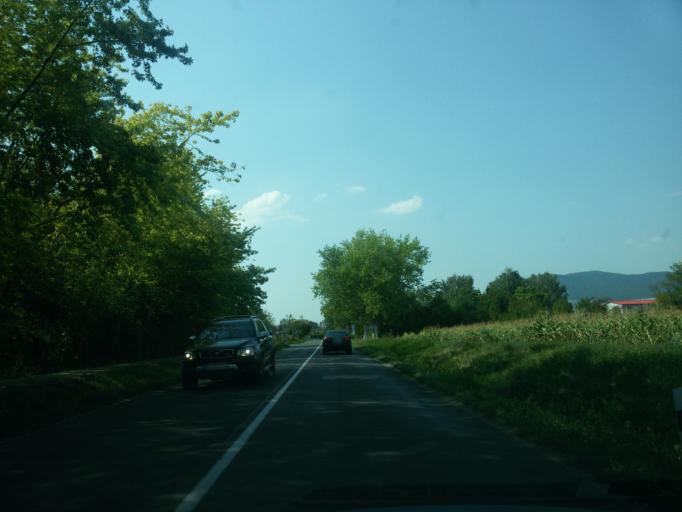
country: SK
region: Nitriansky
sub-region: Okres Nitra
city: Nitra
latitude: 48.3004
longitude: 18.1209
